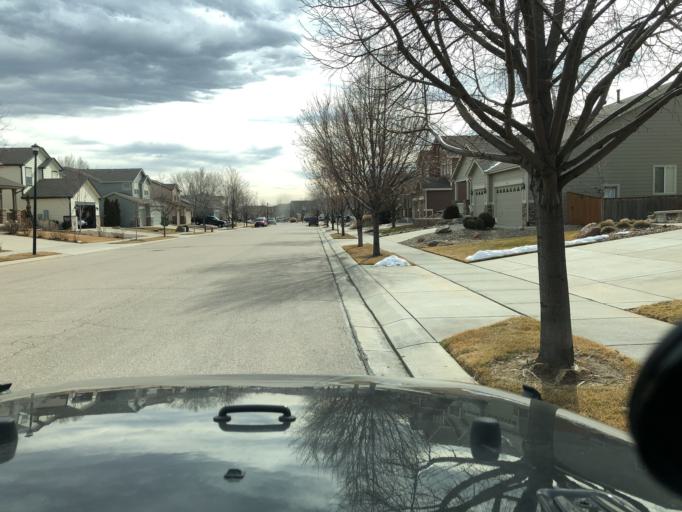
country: US
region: Colorado
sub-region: Boulder County
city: Longmont
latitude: 40.1941
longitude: -105.0669
